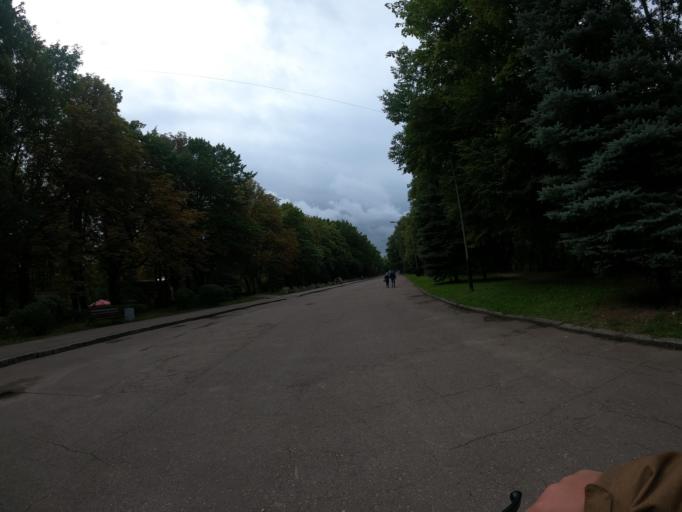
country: RU
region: Kaliningrad
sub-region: Gorod Kaliningrad
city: Kaliningrad
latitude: 54.6944
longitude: 20.5167
